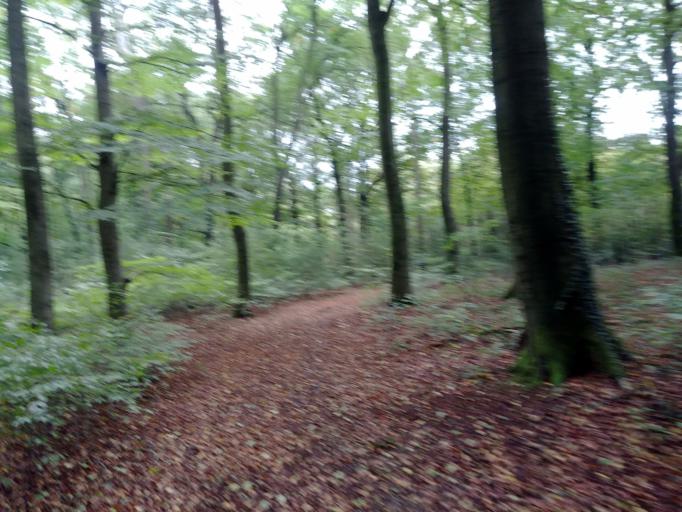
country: NL
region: Gelderland
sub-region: Gemeente Renkum
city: Renkum
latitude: 51.9873
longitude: 5.7253
